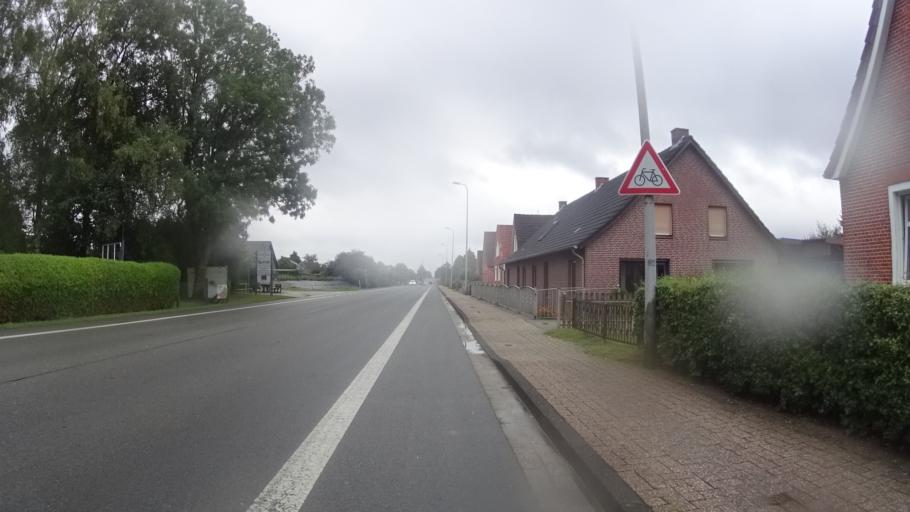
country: DE
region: Lower Saxony
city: Bunde
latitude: 53.1810
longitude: 7.2839
